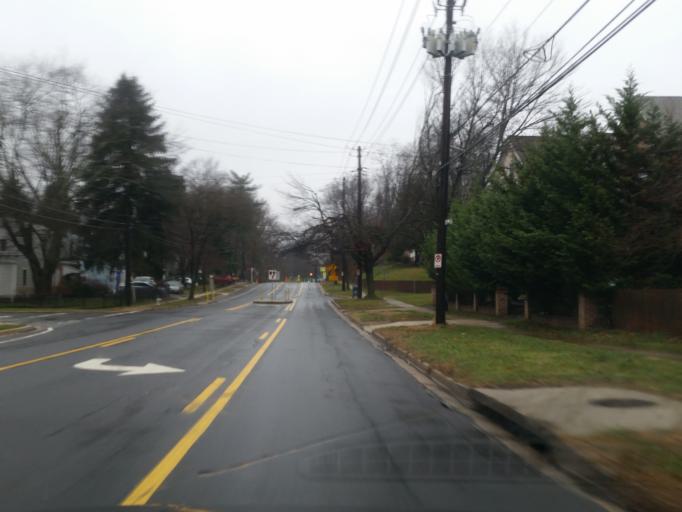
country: US
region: Maryland
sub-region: Montgomery County
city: Forest Glen
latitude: 38.9986
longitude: -77.0678
